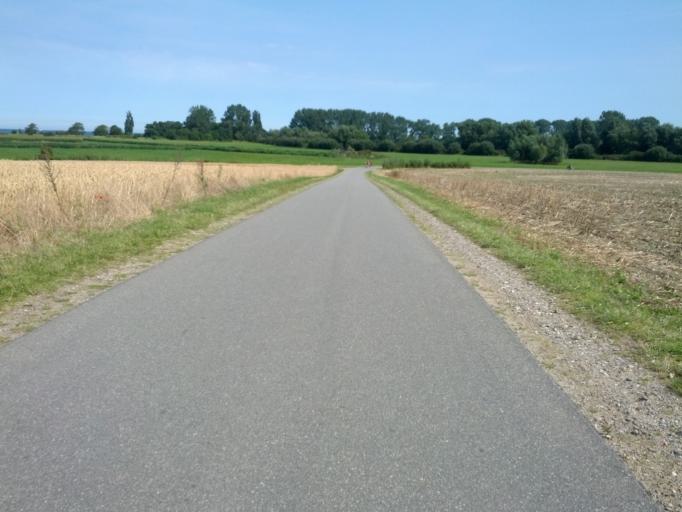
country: DE
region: Mecklenburg-Vorpommern
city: Bastorf
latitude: 54.1477
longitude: 11.6900
